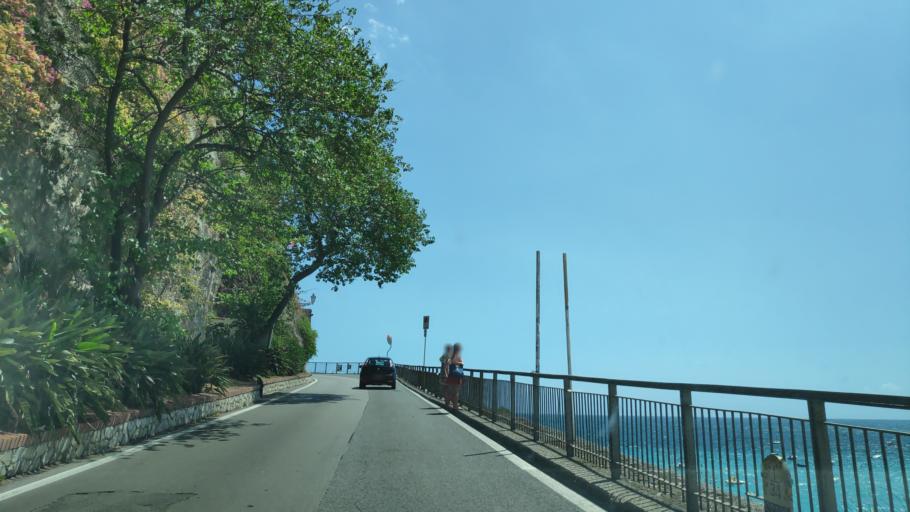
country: IT
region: Campania
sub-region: Provincia di Salerno
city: Minori
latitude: 40.6490
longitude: 14.6296
